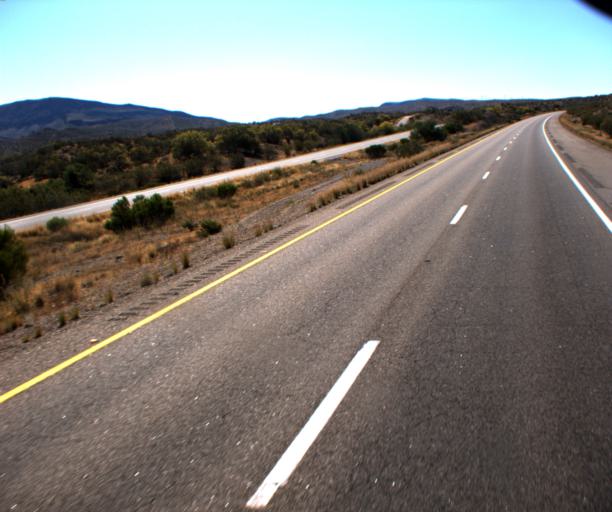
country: US
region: Arizona
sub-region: Yavapai County
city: Bagdad
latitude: 34.6265
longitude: -113.5377
